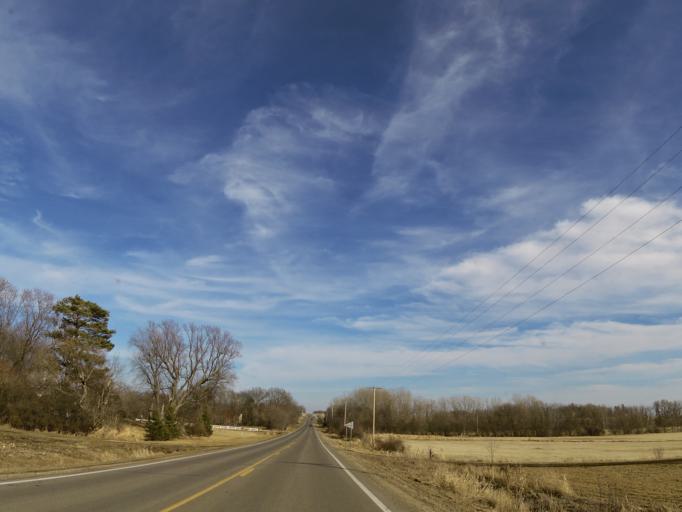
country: US
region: Minnesota
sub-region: Rice County
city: Northfield
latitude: 44.4859
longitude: -93.1917
